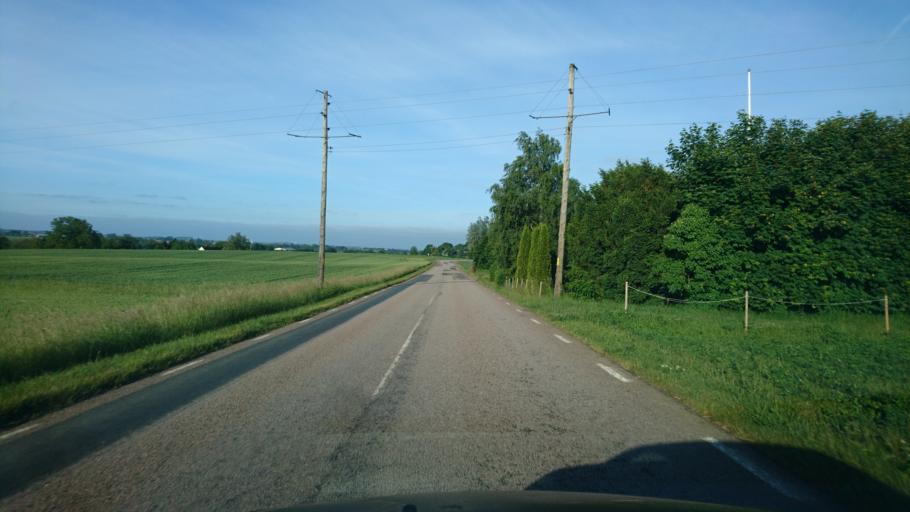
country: SE
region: Skane
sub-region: Tomelilla Kommun
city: Tomelilla
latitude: 55.4507
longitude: 14.1471
